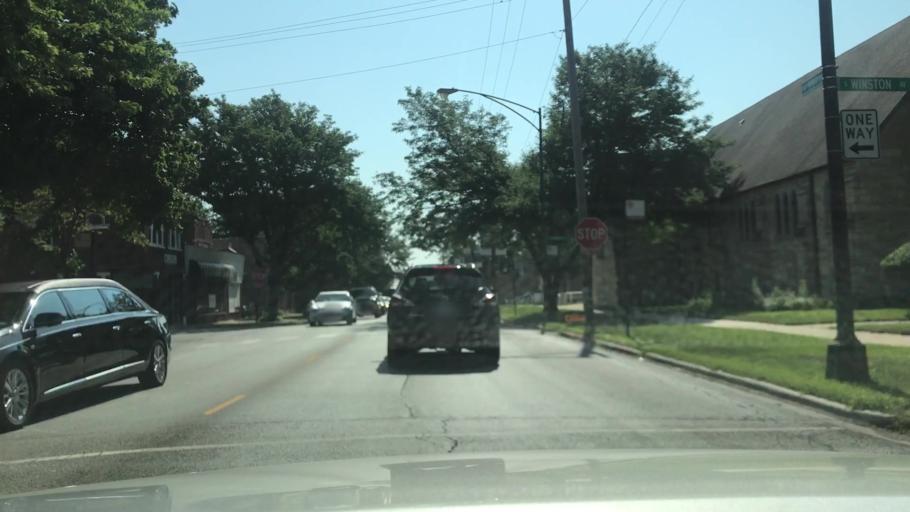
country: US
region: Illinois
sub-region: Cook County
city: Evergreen Park
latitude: 41.7140
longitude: -87.6581
